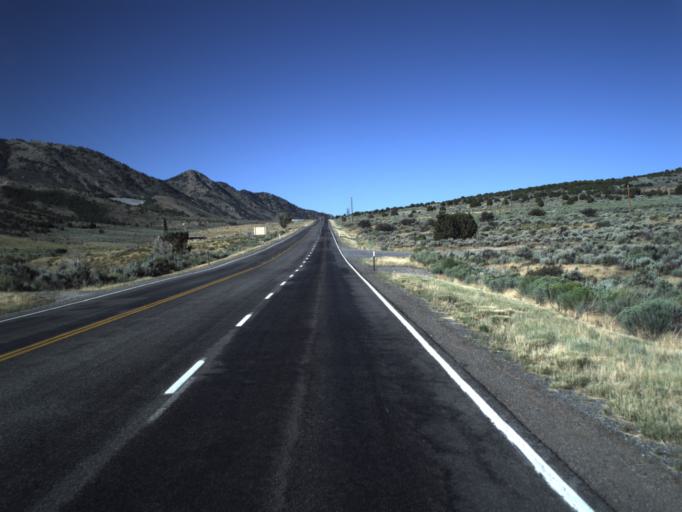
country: US
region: Utah
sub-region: Utah County
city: Genola
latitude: 39.9718
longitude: -112.0848
